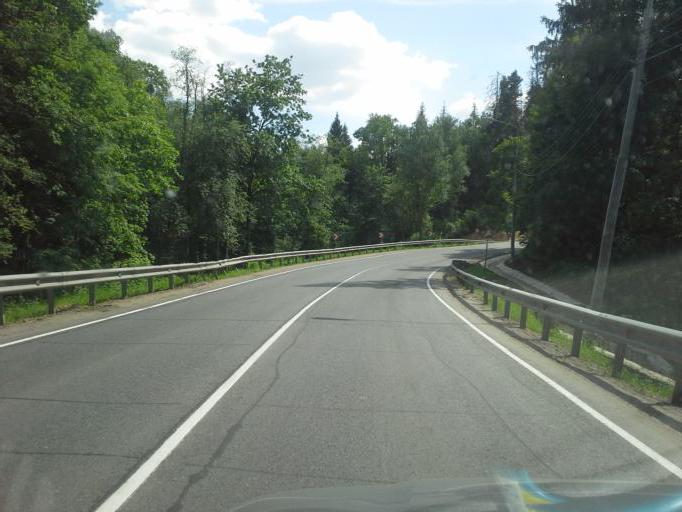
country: RU
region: Moskovskaya
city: Odintsovo
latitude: 55.7065
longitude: 37.2704
